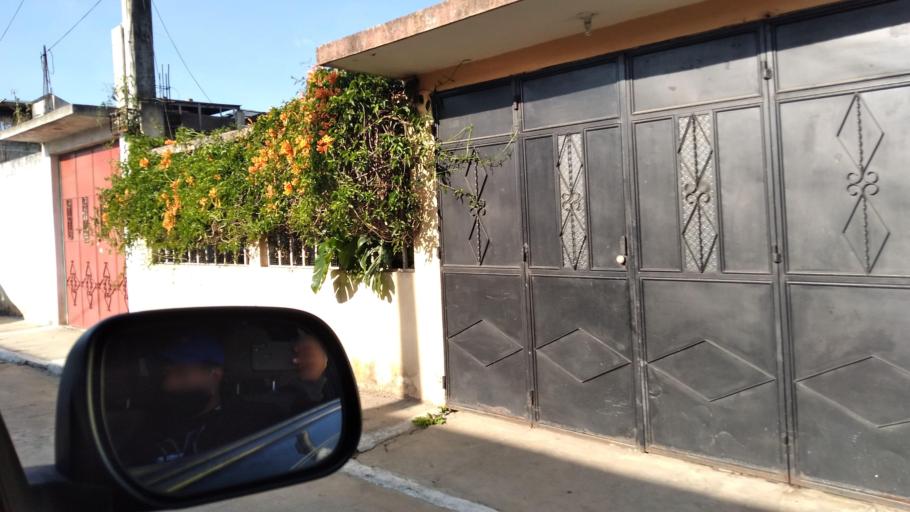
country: GT
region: Quetzaltenango
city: Olintepeque
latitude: 14.8705
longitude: -91.5180
